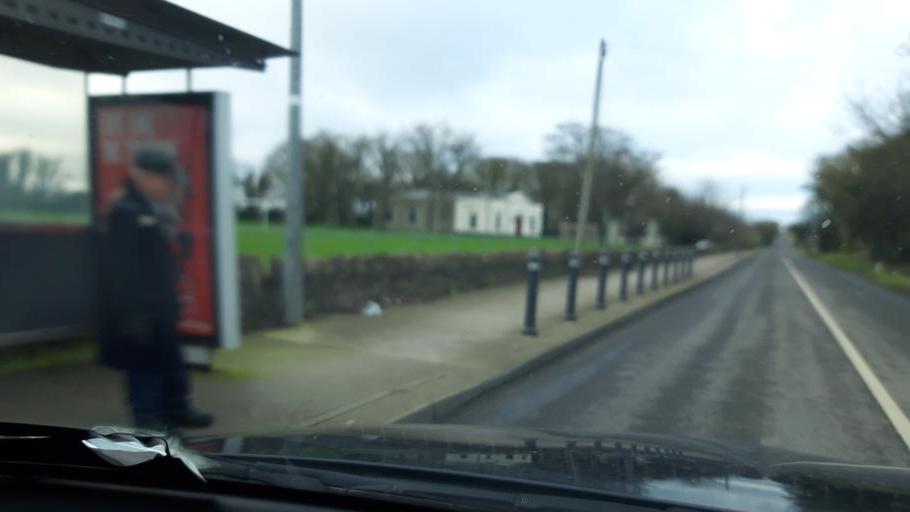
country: IE
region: Leinster
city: An Ros
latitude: 53.5391
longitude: -6.0926
